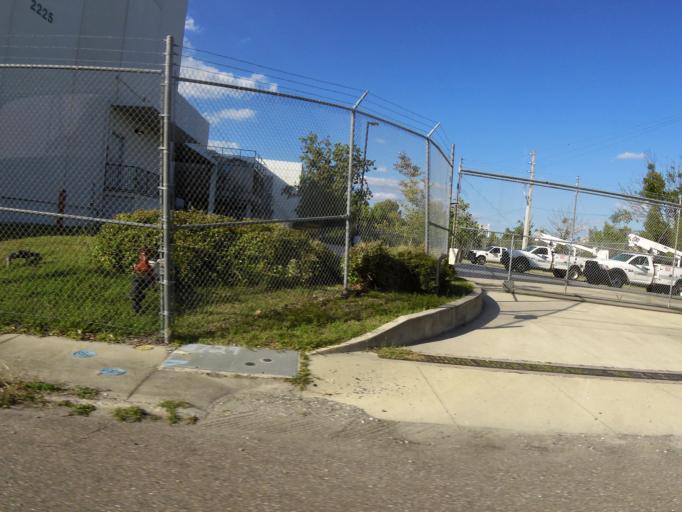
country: US
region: Florida
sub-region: Duval County
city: Jacksonville
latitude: 30.3304
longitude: -81.6852
